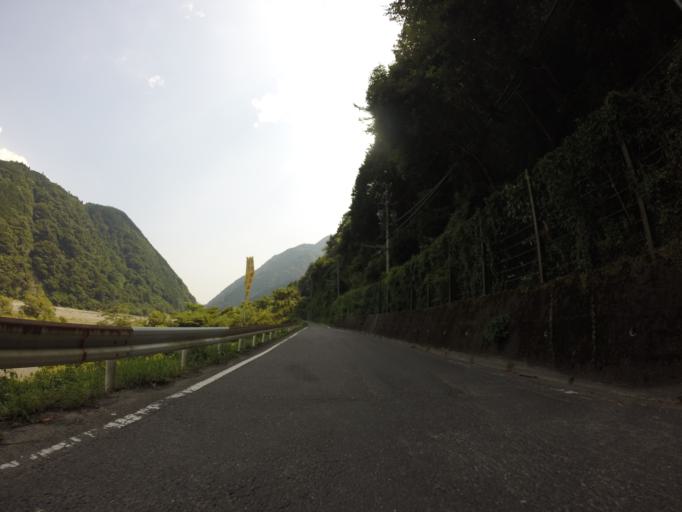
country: JP
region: Shizuoka
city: Shizuoka-shi
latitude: 35.1819
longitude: 138.3610
